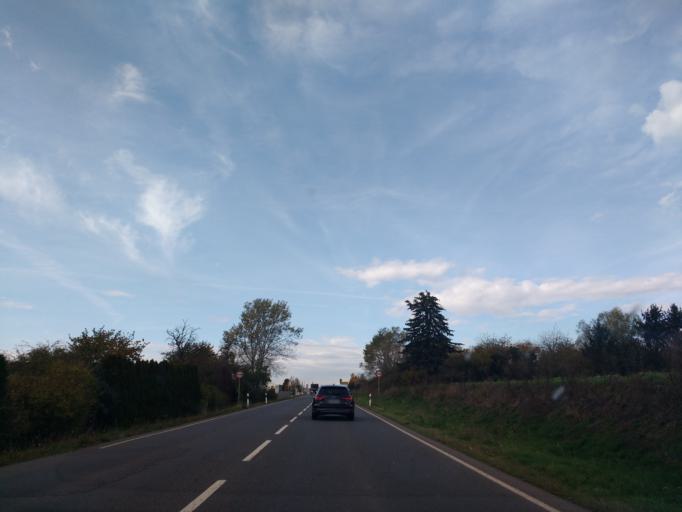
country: DE
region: Thuringia
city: Uthleben
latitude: 51.4881
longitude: 10.8347
